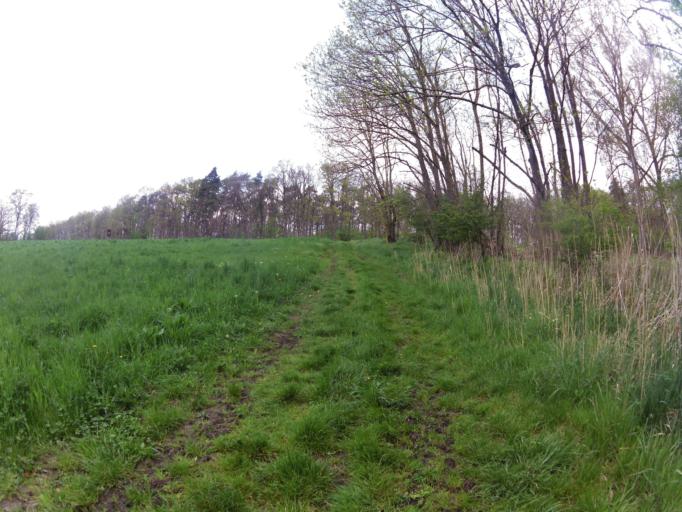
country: DE
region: Bavaria
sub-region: Regierungsbezirk Unterfranken
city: Ochsenfurt
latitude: 49.6992
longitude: 10.0635
